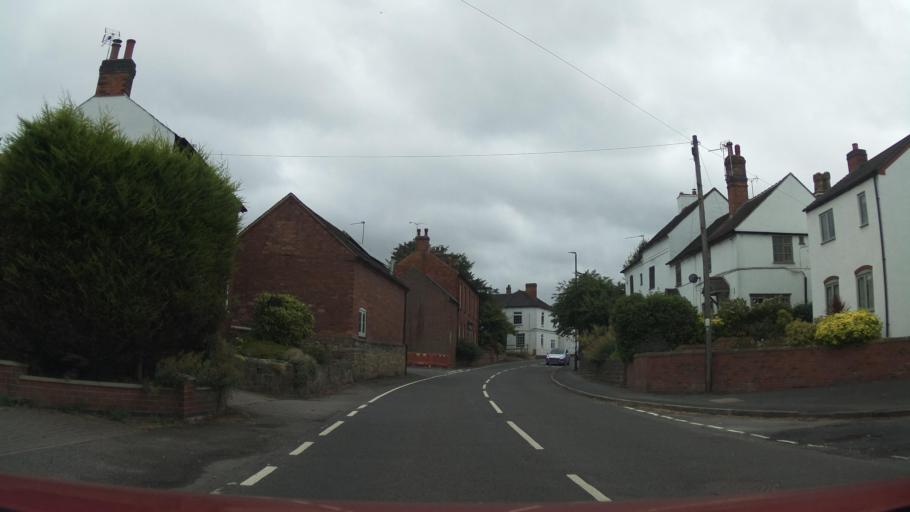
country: GB
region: England
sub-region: Derbyshire
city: Findern
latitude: 52.8731
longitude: -1.5442
